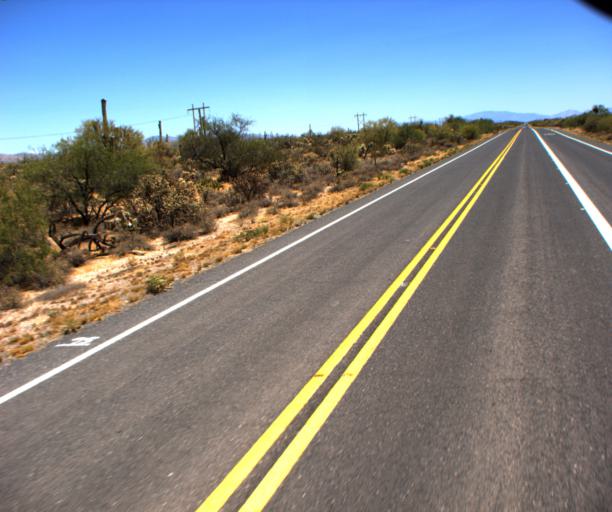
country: US
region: Arizona
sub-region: Pinal County
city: Florence
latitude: 32.8493
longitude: -111.2296
